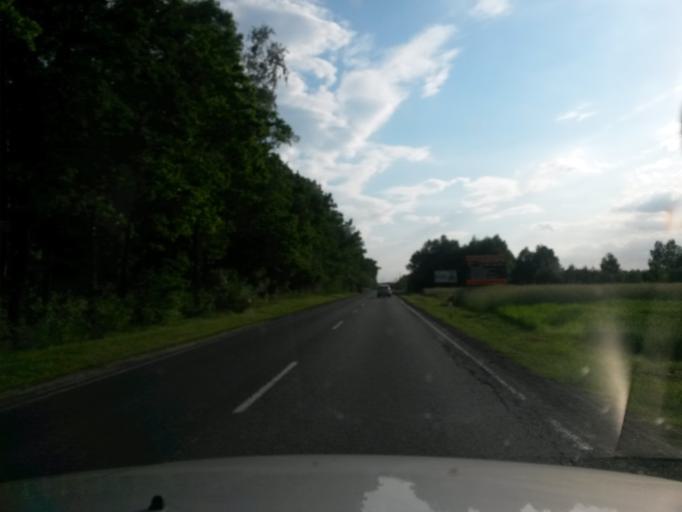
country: PL
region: Lodz Voivodeship
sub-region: Powiat belchatowski
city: Belchatow
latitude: 51.3914
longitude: 19.4025
